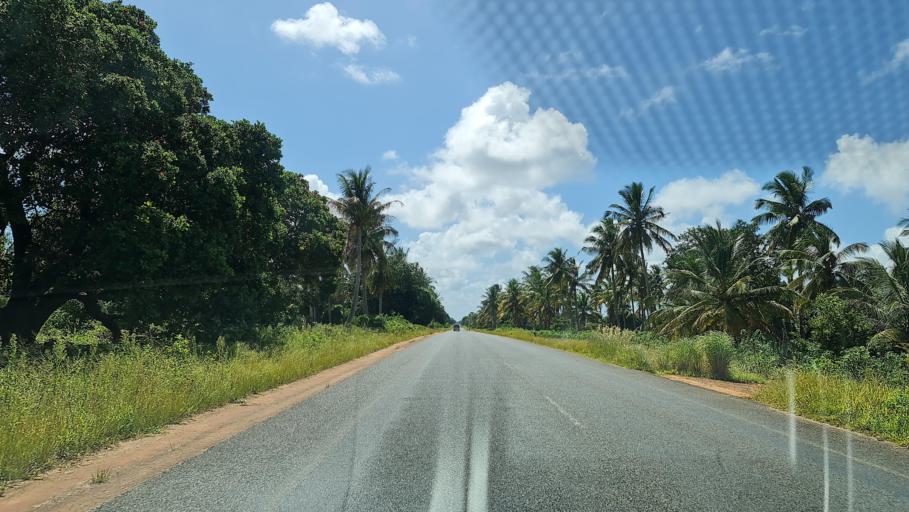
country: MZ
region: Inhambane
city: Maxixe
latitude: -24.5423
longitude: 34.8999
